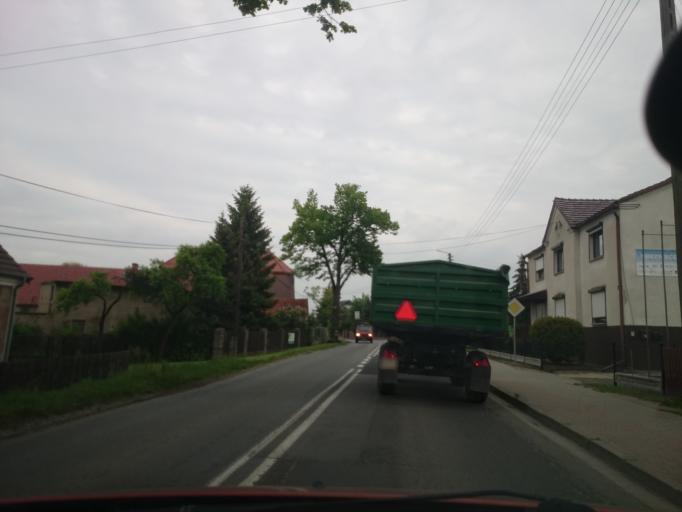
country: PL
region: Opole Voivodeship
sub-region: Powiat opolski
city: Dobrzen Wielki
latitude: 50.7576
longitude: 17.8469
